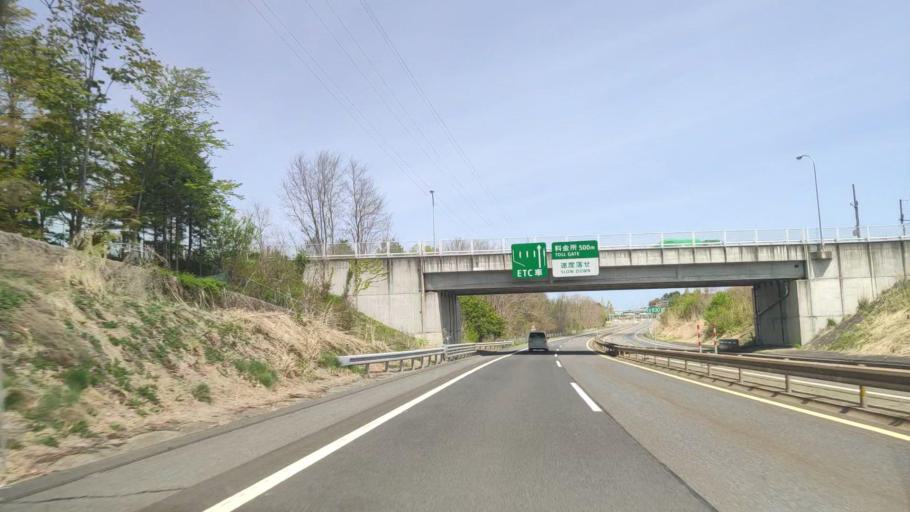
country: JP
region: Aomori
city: Hachinohe
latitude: 40.4816
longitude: 141.4598
